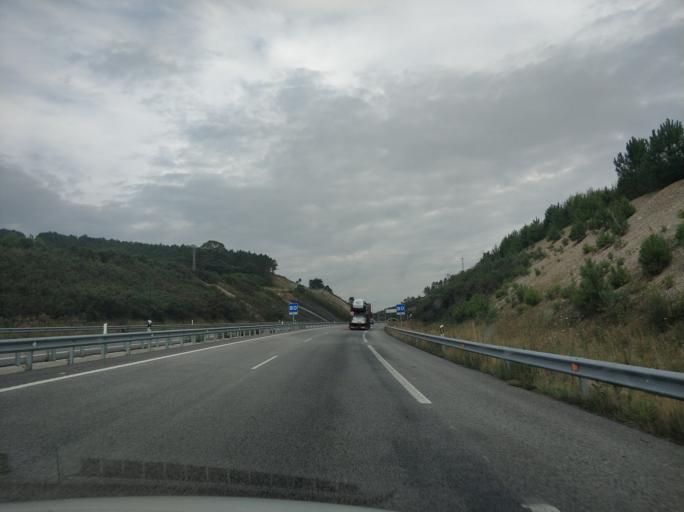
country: ES
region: Asturias
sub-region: Province of Asturias
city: Navia
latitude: 43.5401
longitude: -6.6140
